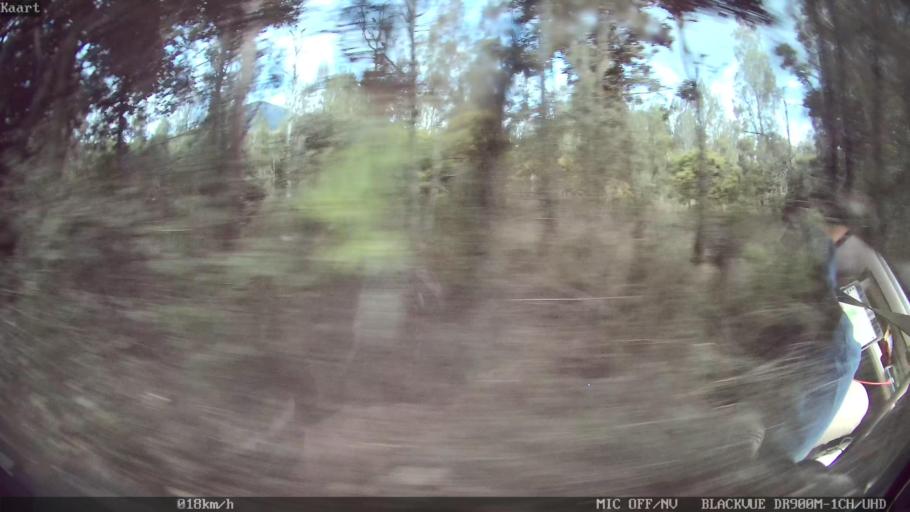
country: ID
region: Bali
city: Banjar Kedisan
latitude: -8.2351
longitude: 115.3559
